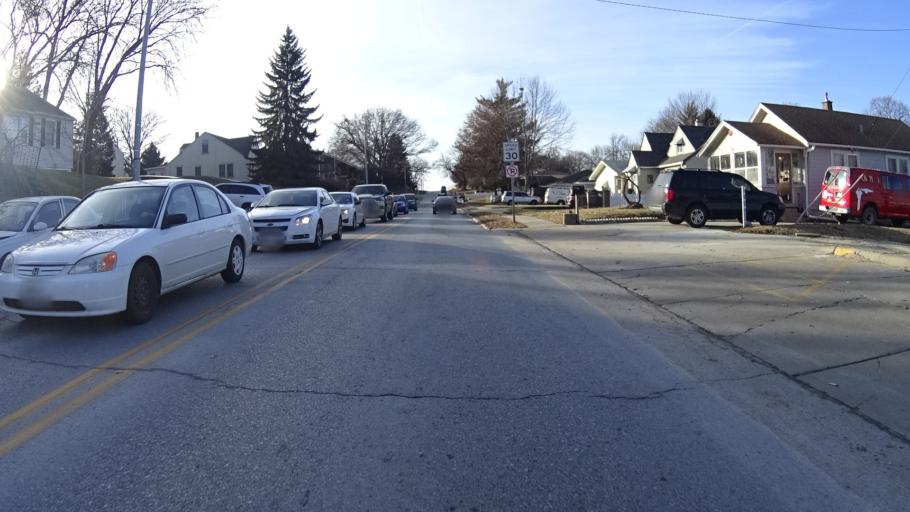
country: US
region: Nebraska
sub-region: Sarpy County
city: La Vista
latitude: 41.1909
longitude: -95.9678
